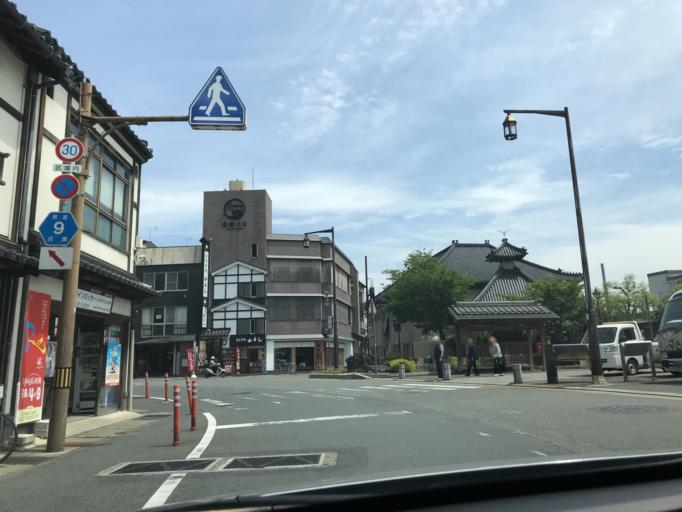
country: JP
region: Hyogo
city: Toyooka
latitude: 35.6237
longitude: 134.8131
